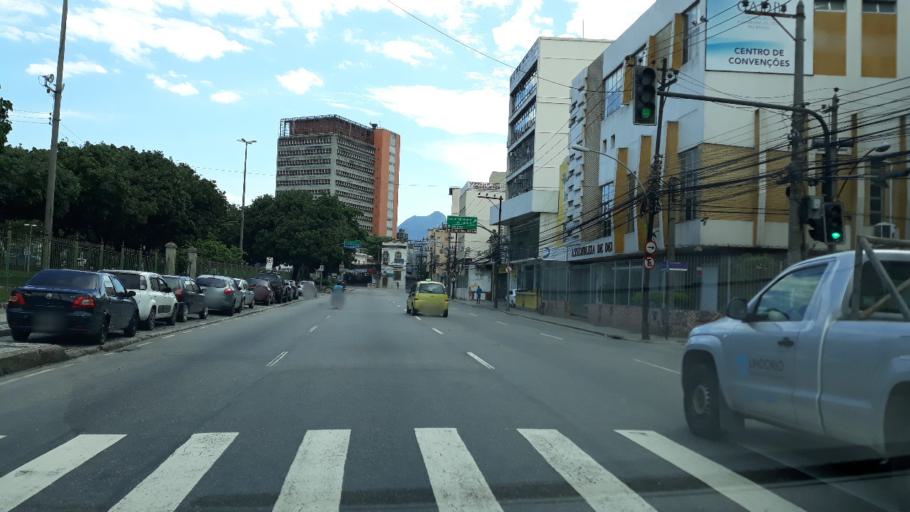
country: BR
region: Rio de Janeiro
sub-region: Rio De Janeiro
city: Rio de Janeiro
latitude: -22.8977
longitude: -43.2223
